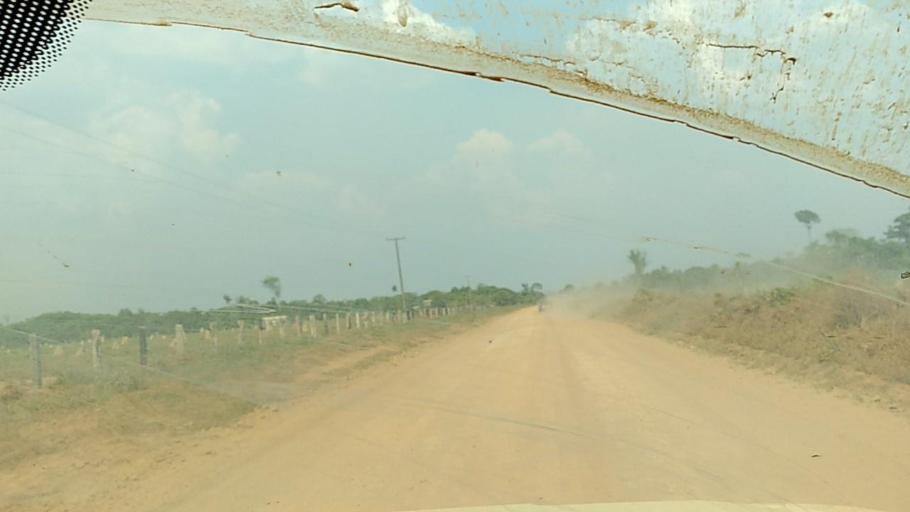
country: BR
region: Rondonia
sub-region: Porto Velho
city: Porto Velho
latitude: -8.6832
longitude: -63.2117
